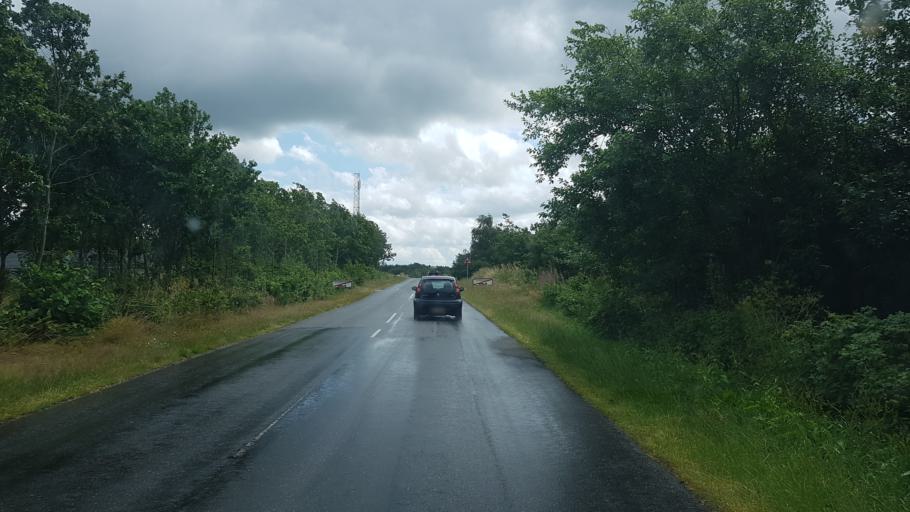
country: DK
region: South Denmark
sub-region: Kolding Kommune
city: Lunderskov
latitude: 55.4704
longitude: 9.2900
